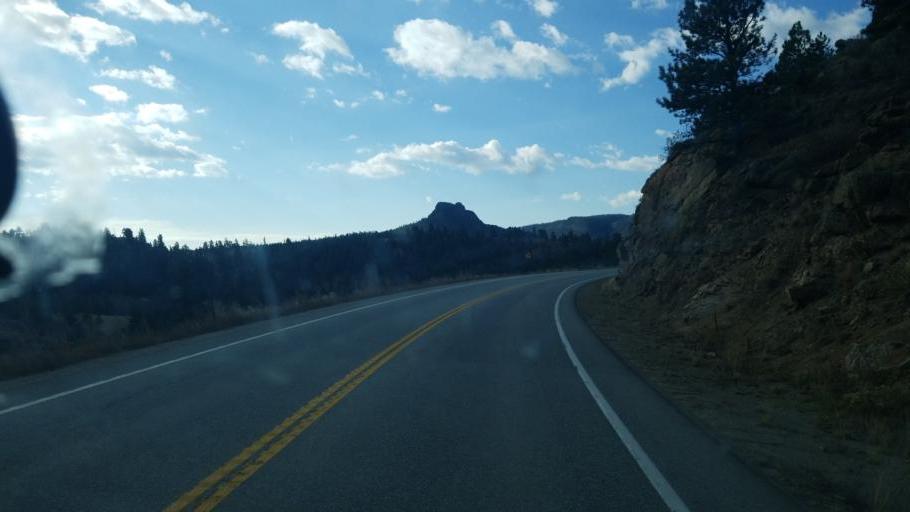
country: US
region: Colorado
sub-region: Chaffee County
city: Buena Vista
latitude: 38.8527
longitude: -105.9834
